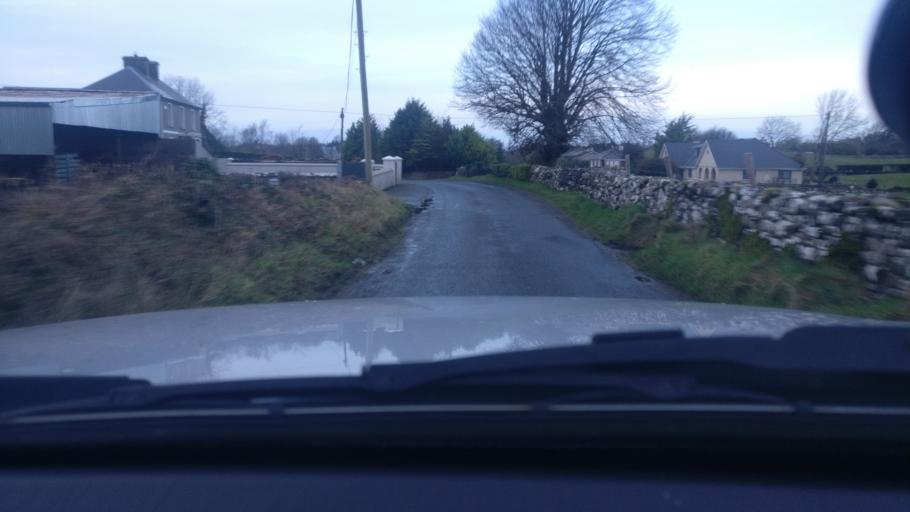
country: IE
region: Connaught
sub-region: County Galway
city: Loughrea
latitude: 53.1798
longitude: -8.5954
